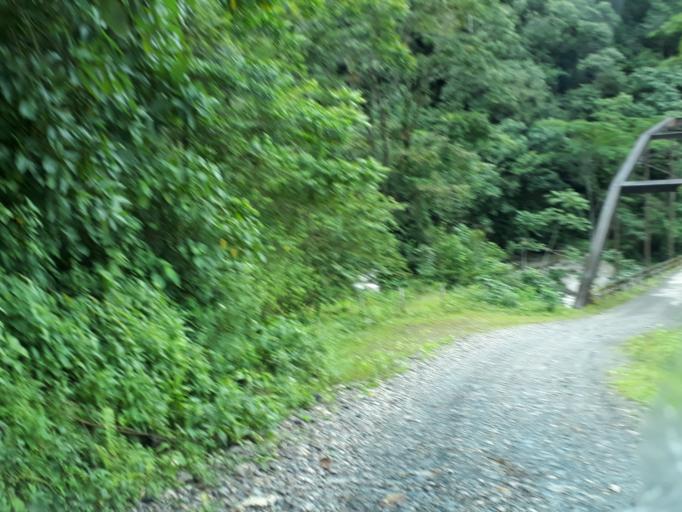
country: CO
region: Cundinamarca
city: Gachala
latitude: 4.7203
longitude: -73.3604
